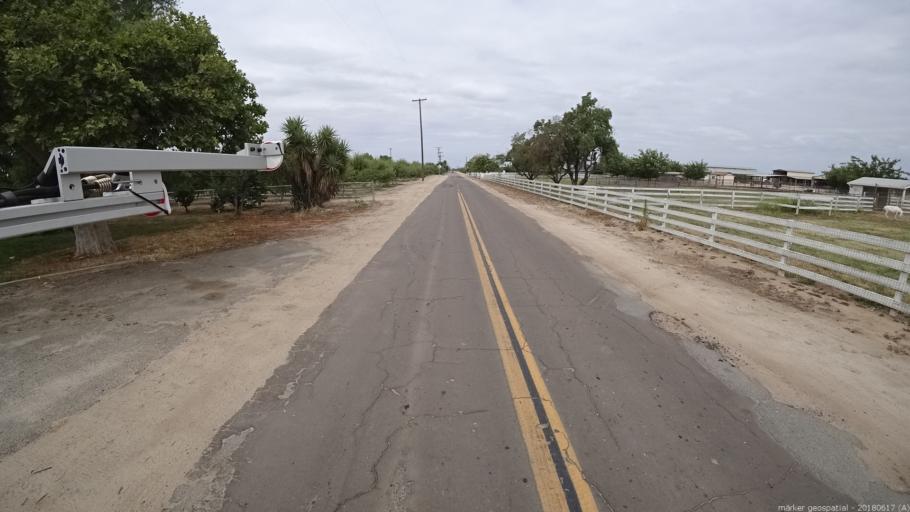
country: US
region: California
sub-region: Madera County
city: Fairmead
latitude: 37.0037
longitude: -120.2030
